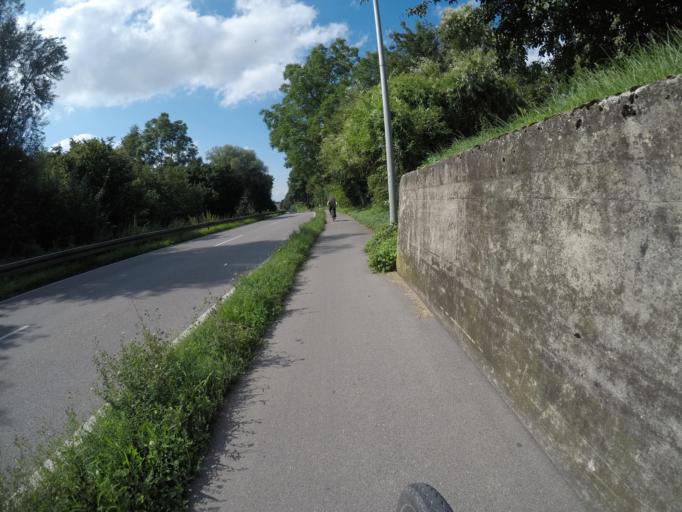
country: DE
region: Baden-Wuerttemberg
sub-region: Regierungsbezirk Stuttgart
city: Unterensingen
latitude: 48.6477
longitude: 9.3520
